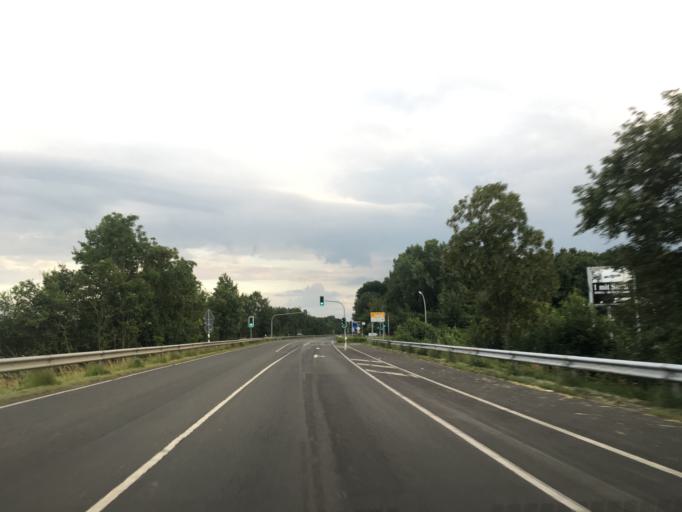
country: DE
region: North Rhine-Westphalia
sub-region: Regierungsbezirk Munster
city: Senden
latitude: 51.9062
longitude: 7.4913
